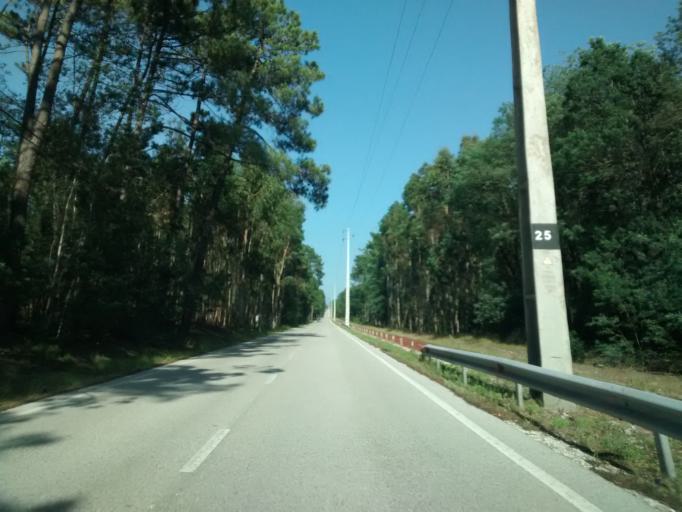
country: PT
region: Leiria
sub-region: Leiria
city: Monte Redondo
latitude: 39.9798
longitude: -8.8307
